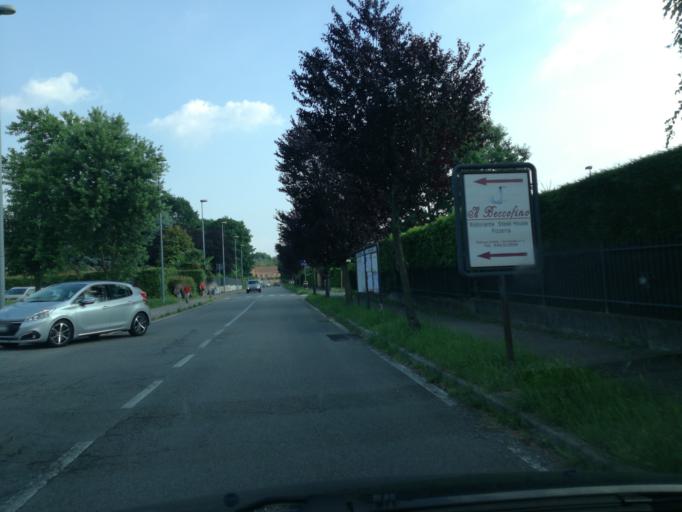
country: IT
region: Lombardy
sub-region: Provincia di Lecco
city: Paderno d'Adda
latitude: 45.6822
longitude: 9.4408
